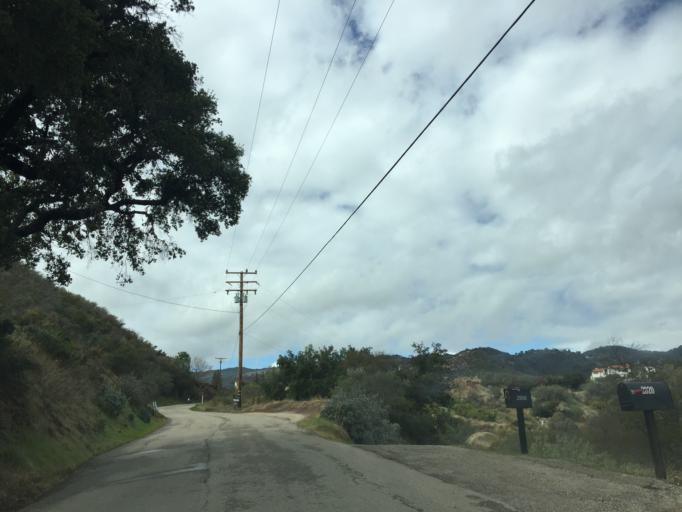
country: US
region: California
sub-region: Santa Barbara County
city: Goleta
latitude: 34.4788
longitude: -119.7962
